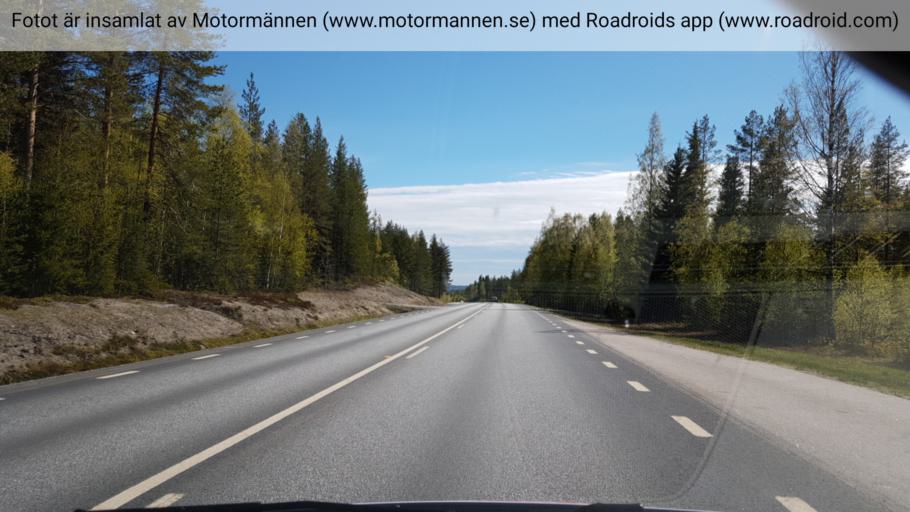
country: SE
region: Vaesterbotten
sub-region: Vannas Kommun
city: Vannasby
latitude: 64.0508
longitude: 19.9979
